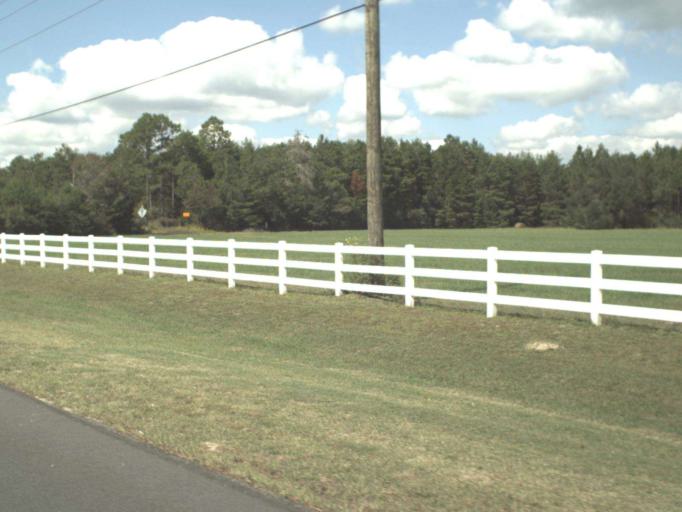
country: US
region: Florida
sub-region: Walton County
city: Freeport
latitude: 30.5082
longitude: -86.1654
